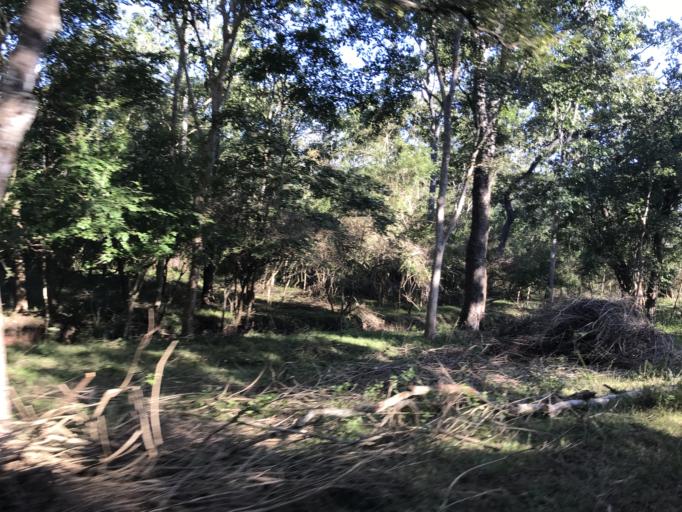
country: IN
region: Karnataka
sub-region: Mysore
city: Heggadadevankote
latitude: 11.9822
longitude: 76.2327
